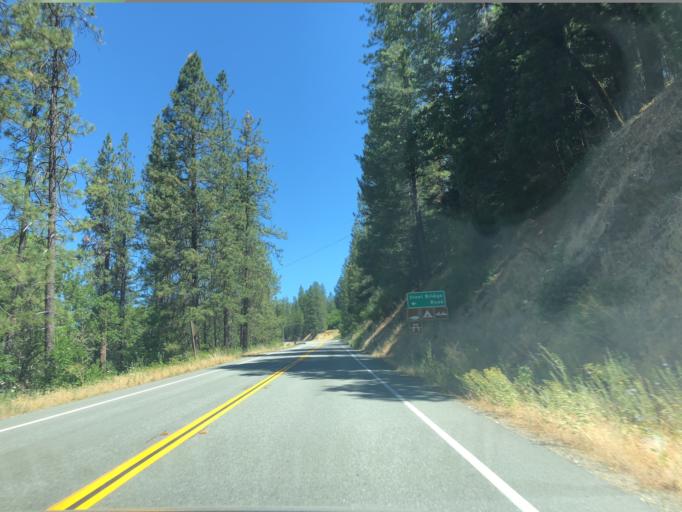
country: US
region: California
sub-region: Trinity County
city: Weaverville
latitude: 40.6558
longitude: -122.8960
